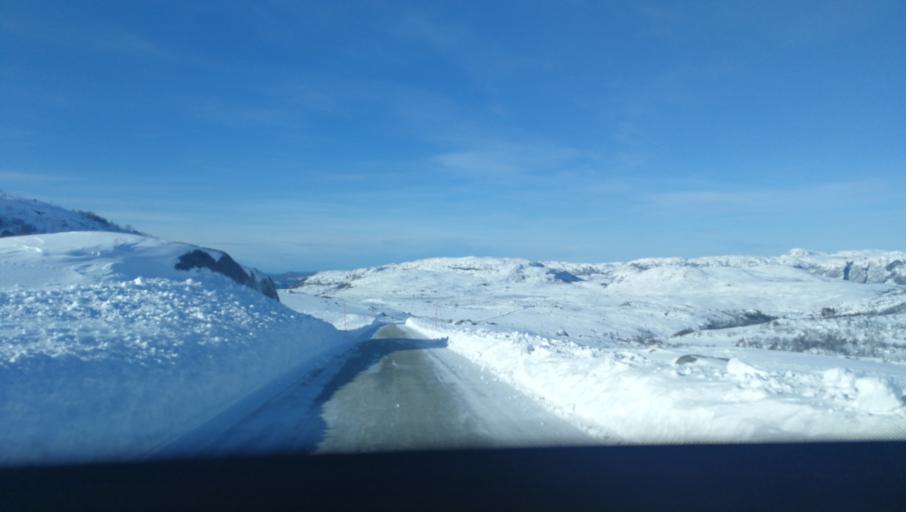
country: NO
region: Rogaland
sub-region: Hjelmeland
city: Hjelmelandsvagen
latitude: 59.1006
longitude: 6.3870
